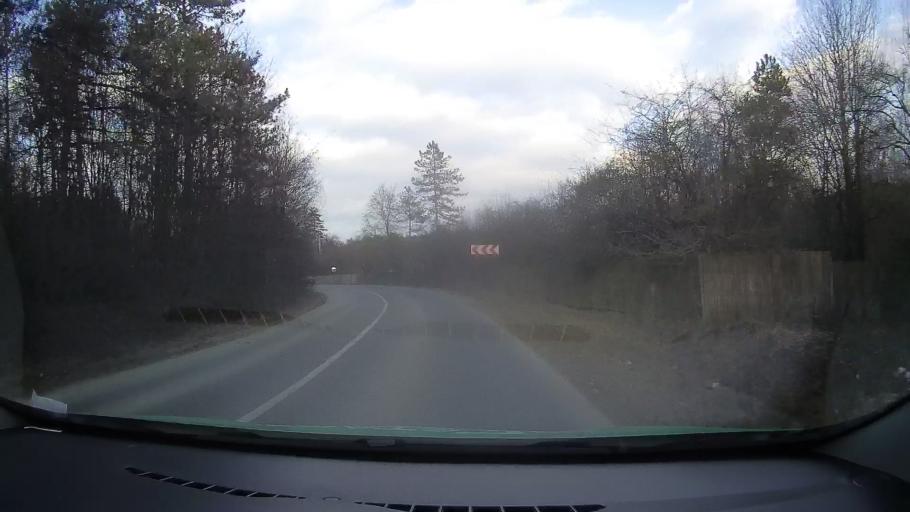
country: RO
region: Dambovita
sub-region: Comuna Gura Ocnitei
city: Gura Ocnitei
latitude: 44.9498
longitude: 25.5948
